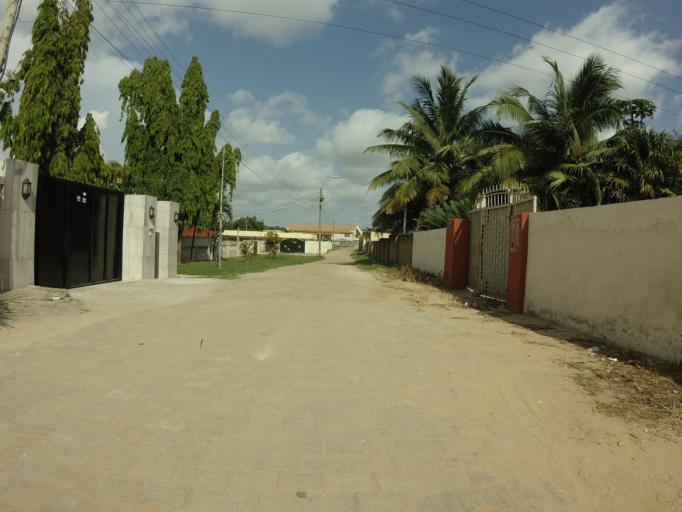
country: GH
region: Greater Accra
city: Dome
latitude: 5.6183
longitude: -0.2386
